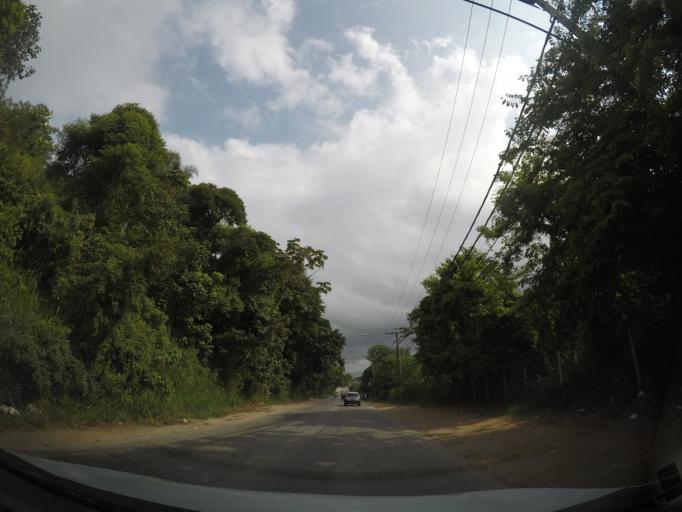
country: BR
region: Sao Paulo
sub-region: Aruja
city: Aruja
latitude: -23.4184
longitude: -46.4085
